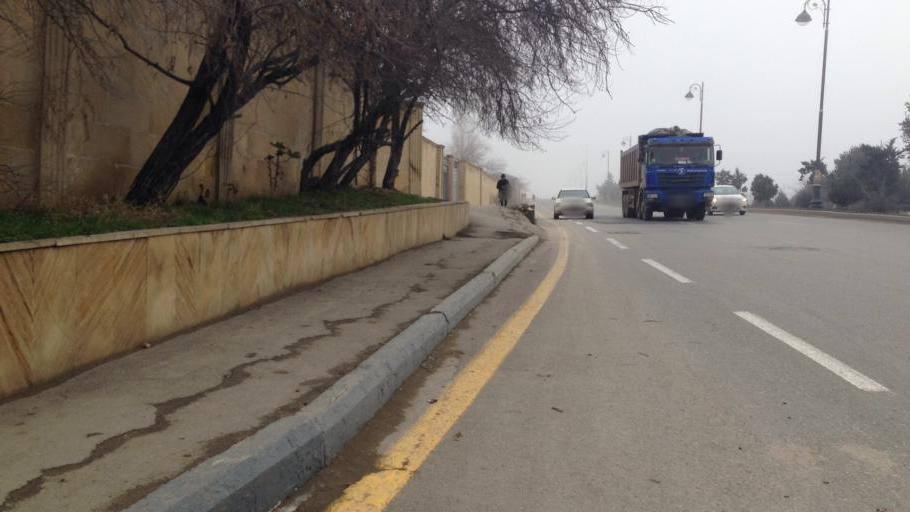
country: AZ
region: Baki
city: Qaracuxur
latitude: 40.3519
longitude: 49.9592
